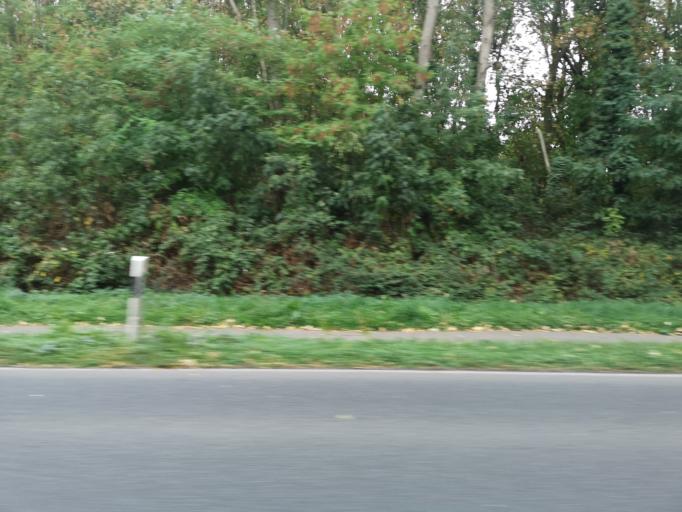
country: DE
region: North Rhine-Westphalia
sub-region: Regierungsbezirk Koln
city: Dueren
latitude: 50.7823
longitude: 6.4883
